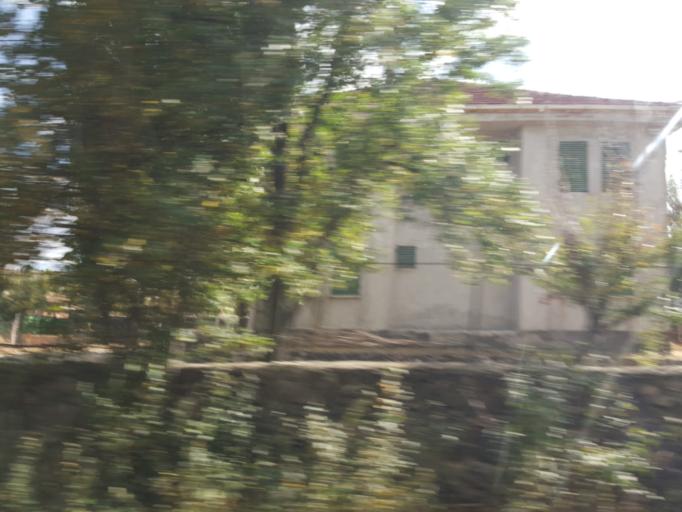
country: TR
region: Tokat
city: Sulusaray
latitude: 39.9888
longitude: 35.9941
